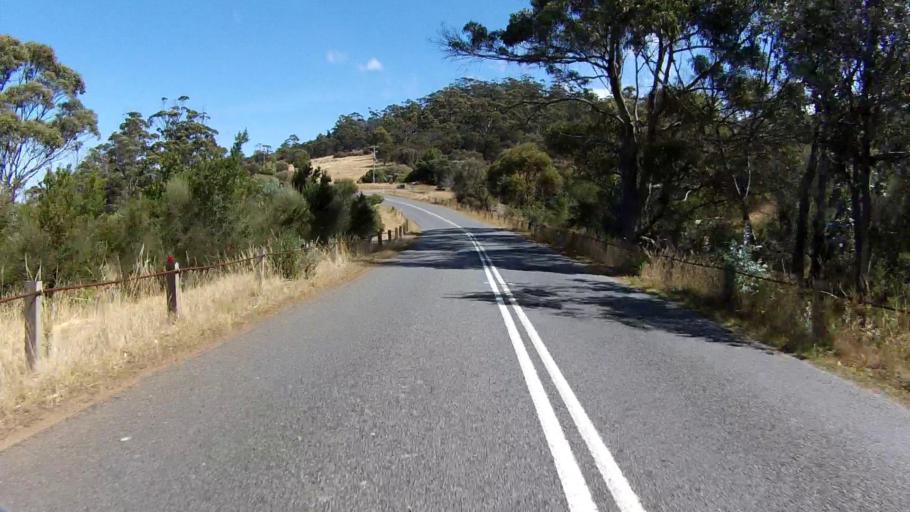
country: AU
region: Tasmania
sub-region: Sorell
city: Sorell
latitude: -42.2334
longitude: 148.0181
